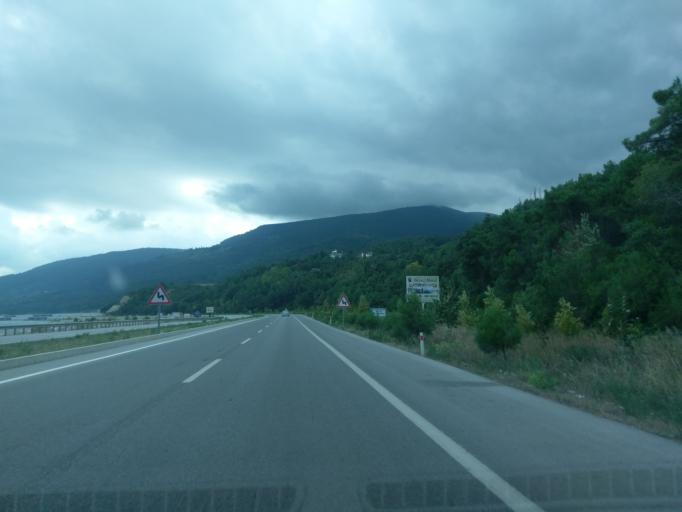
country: TR
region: Sinop
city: Gerze
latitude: 41.7774
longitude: 35.2026
